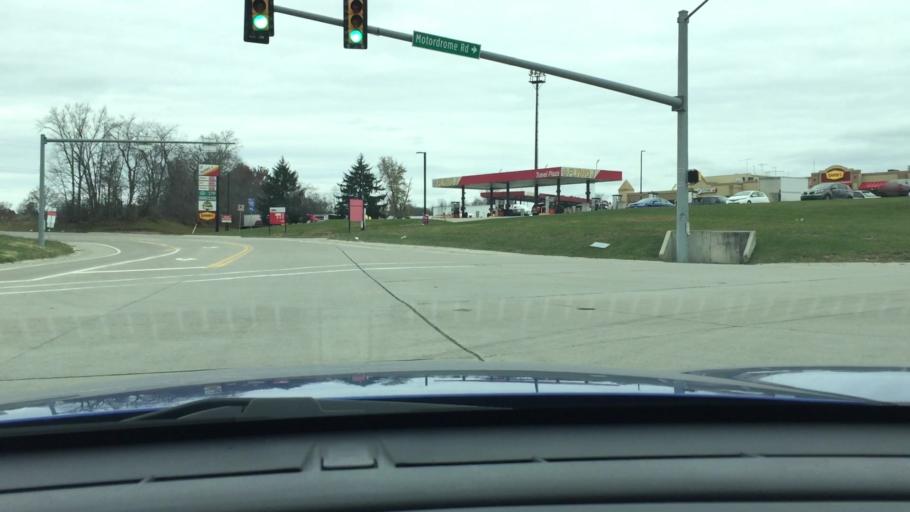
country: US
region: Pennsylvania
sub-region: Westmoreland County
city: West Newton
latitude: 40.1689
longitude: -79.7326
